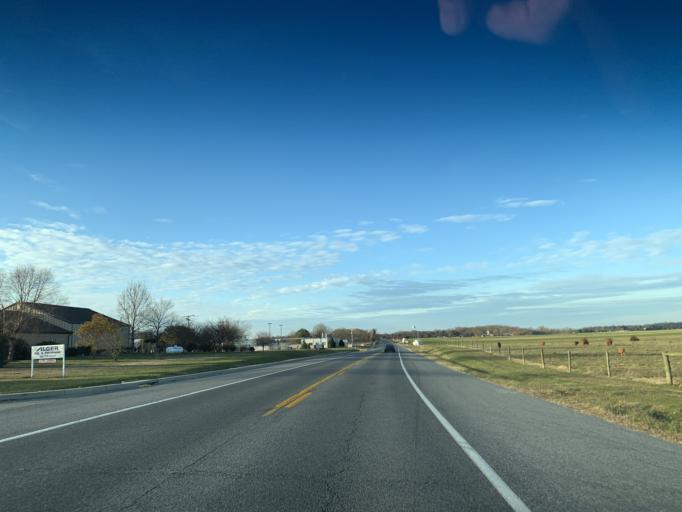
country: US
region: Maryland
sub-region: Kent County
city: Chestertown
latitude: 39.2608
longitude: -76.0856
